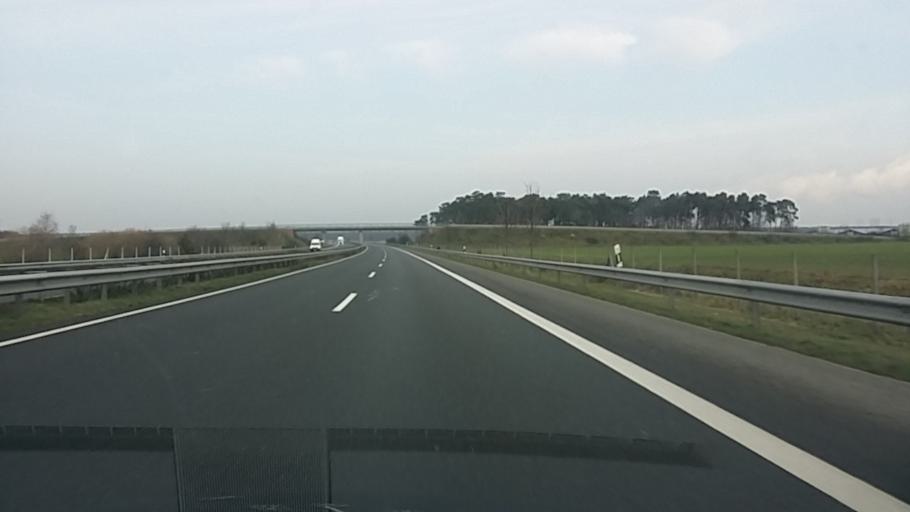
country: DE
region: Lower Saxony
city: Emsburen
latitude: 52.4277
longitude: 7.2601
